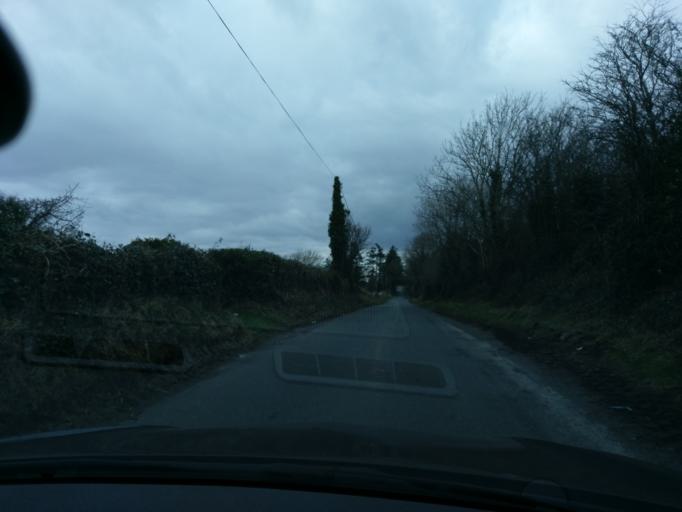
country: IE
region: Connaught
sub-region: County Galway
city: Athenry
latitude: 53.4559
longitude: -8.5833
